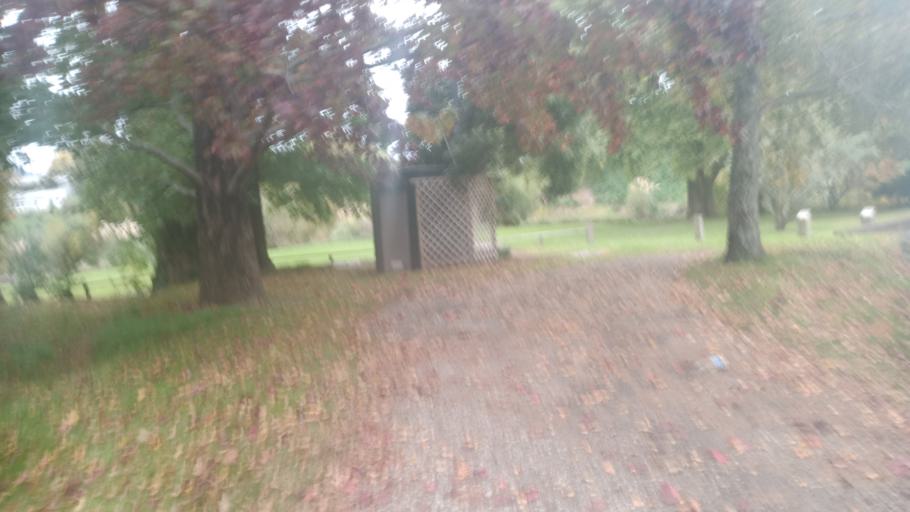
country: NZ
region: Gisborne
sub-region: Gisborne District
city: Gisborne
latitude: -38.6660
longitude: 178.0398
